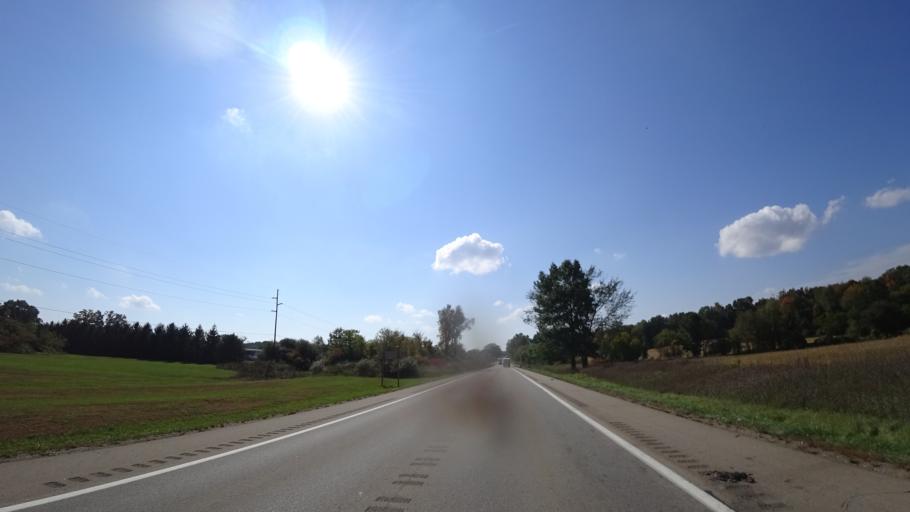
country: US
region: Michigan
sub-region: Jackson County
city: Concord
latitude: 42.1732
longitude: -84.6603
